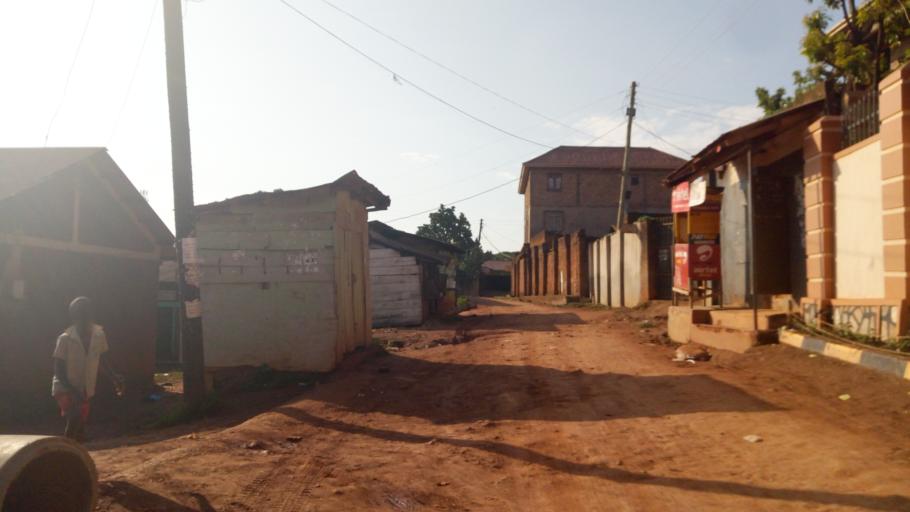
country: UG
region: Central Region
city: Kampala Central Division
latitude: 0.3367
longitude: 32.5607
